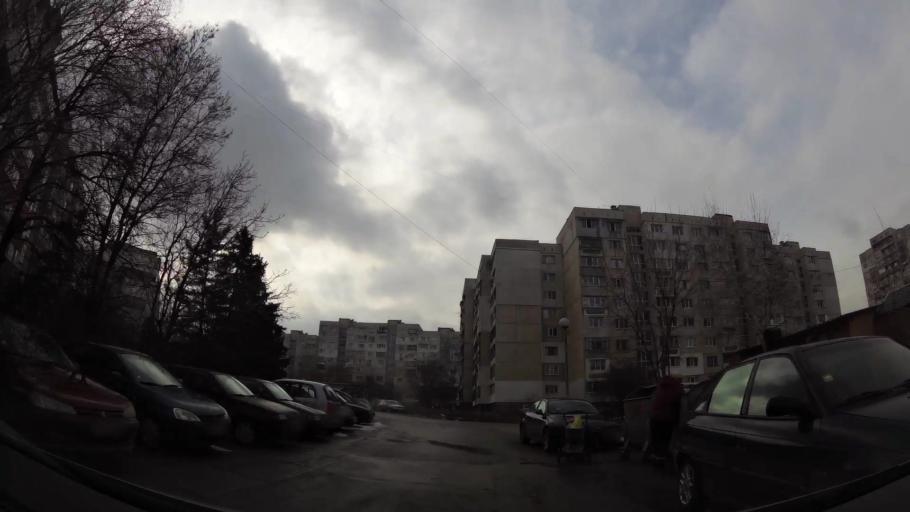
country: BG
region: Sofiya
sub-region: Obshtina Bozhurishte
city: Bozhurishte
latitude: 42.7161
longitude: 23.2383
